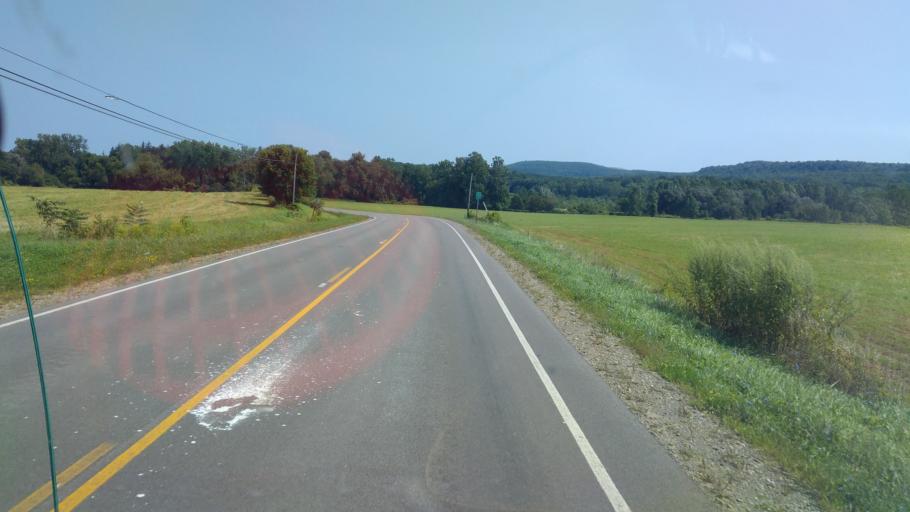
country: US
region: New York
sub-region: Allegany County
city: Belmont
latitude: 42.2596
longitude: -78.0538
